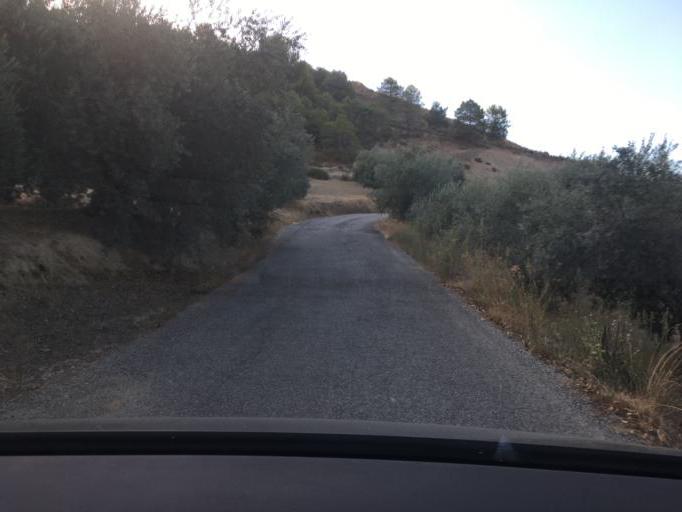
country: ES
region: Andalusia
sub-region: Provincia de Granada
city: Beas de Granada
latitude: 37.2105
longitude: -3.4649
